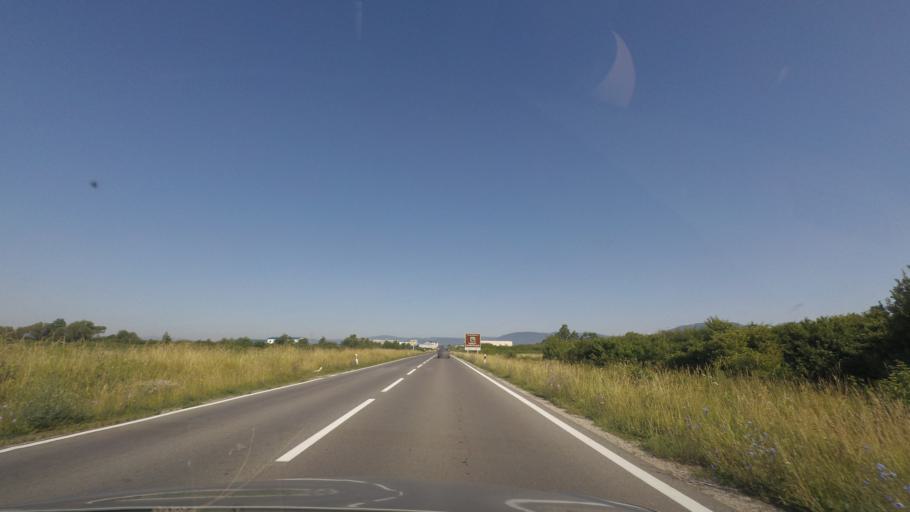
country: HR
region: Zagrebacka
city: Jastrebarsko
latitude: 45.6480
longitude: 15.6690
